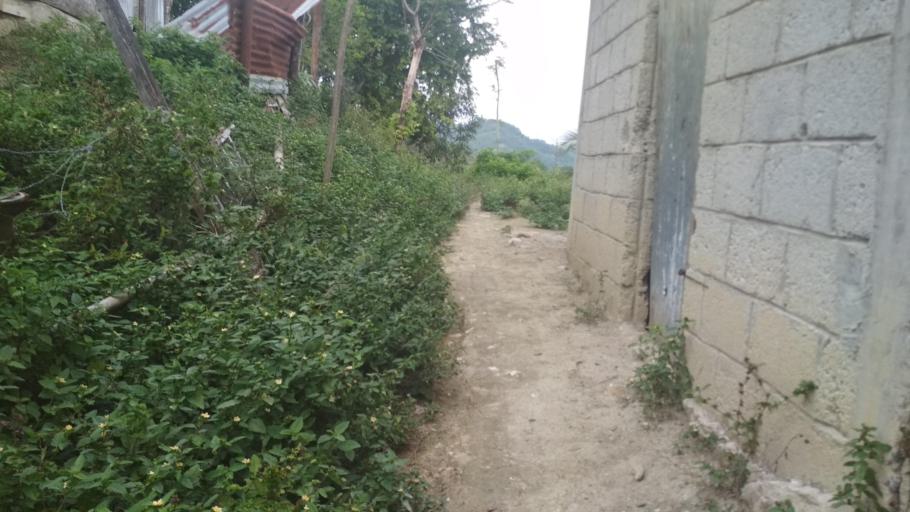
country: MX
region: Veracruz
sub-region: Poza Rica de Hidalgo
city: El Mollejon
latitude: 20.5244
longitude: -97.3763
